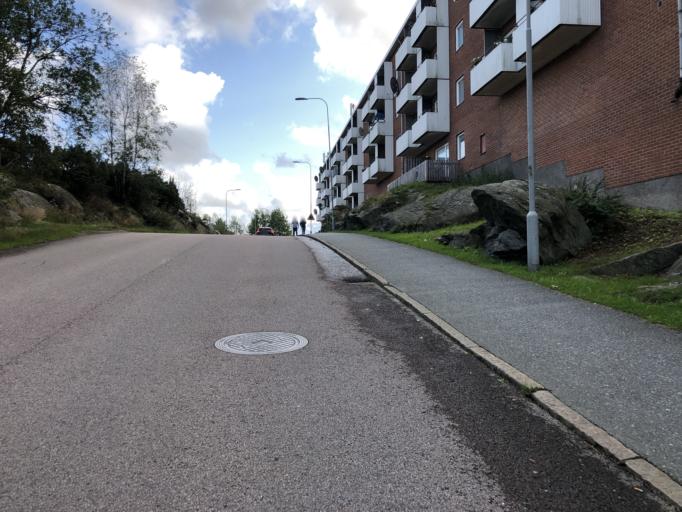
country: SE
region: Vaestra Goetaland
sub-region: Goteborg
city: Majorna
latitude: 57.7322
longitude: 11.8939
